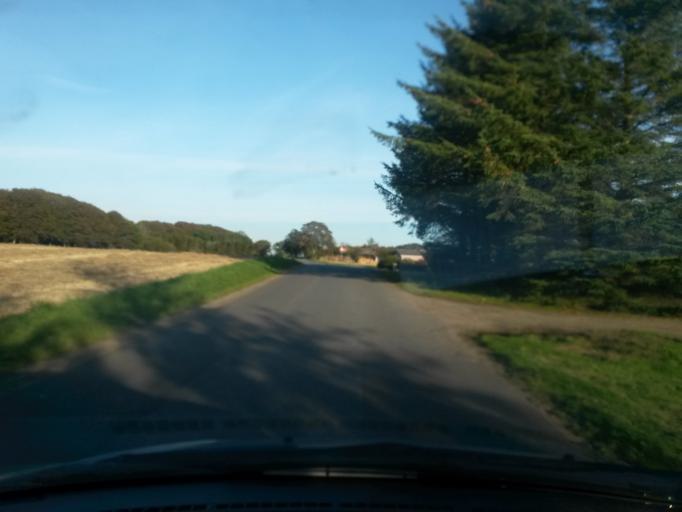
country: DK
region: Central Jutland
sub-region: Silkeborg Kommune
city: Kjellerup
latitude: 56.3174
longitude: 9.3923
